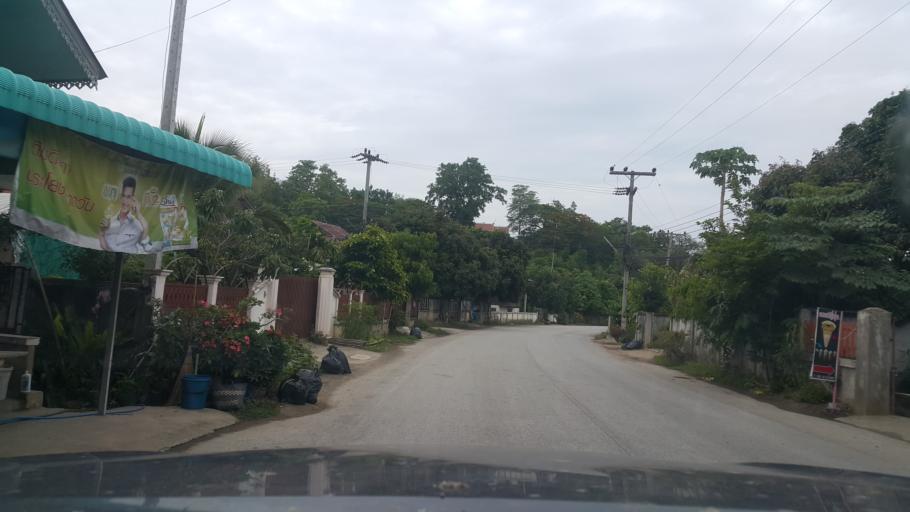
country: TH
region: Chiang Mai
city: San Pa Tong
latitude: 18.6573
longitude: 98.8369
